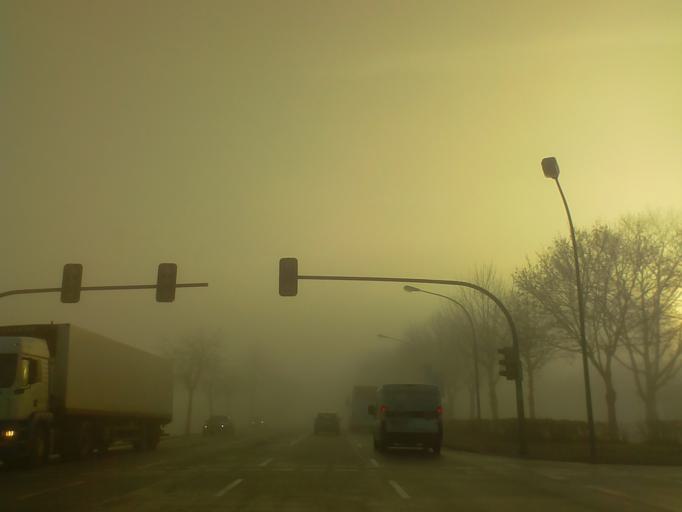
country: DE
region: Hesse
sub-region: Regierungsbezirk Darmstadt
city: Heppenheim an der Bergstrasse
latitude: 49.6451
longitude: 8.6175
